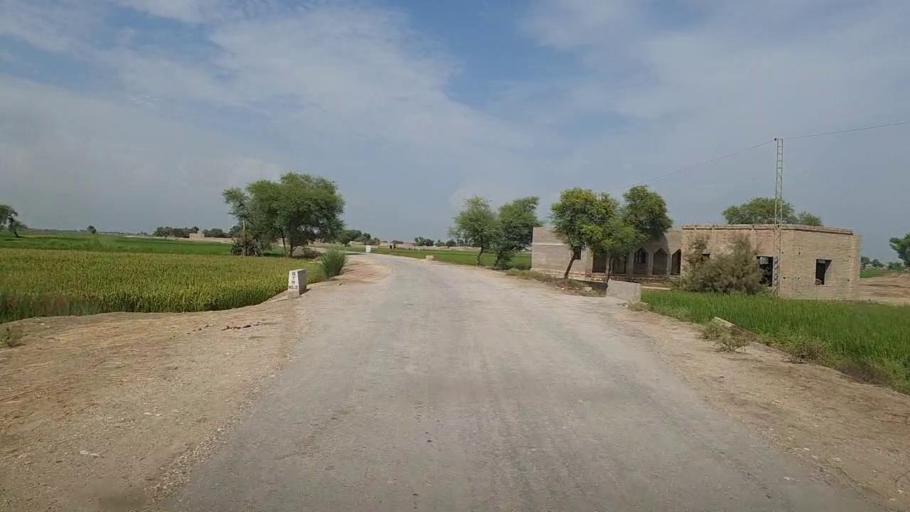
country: PK
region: Sindh
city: Thul
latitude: 28.2636
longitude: 68.8167
